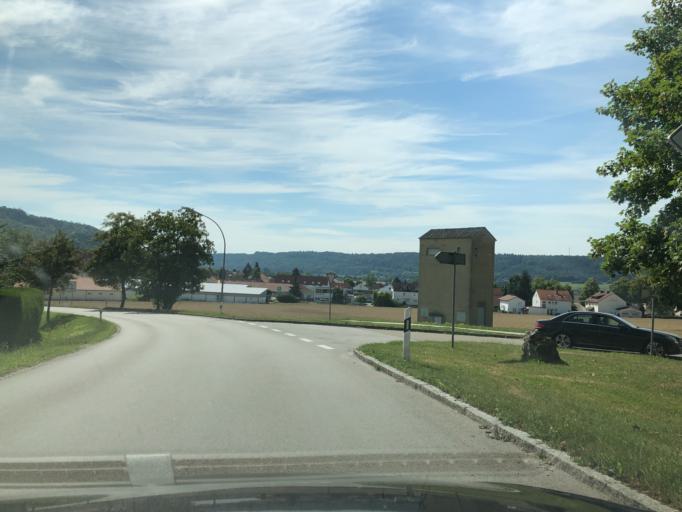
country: DE
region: Bavaria
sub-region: Upper Palatinate
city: Berching
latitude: 49.0376
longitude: 11.4654
